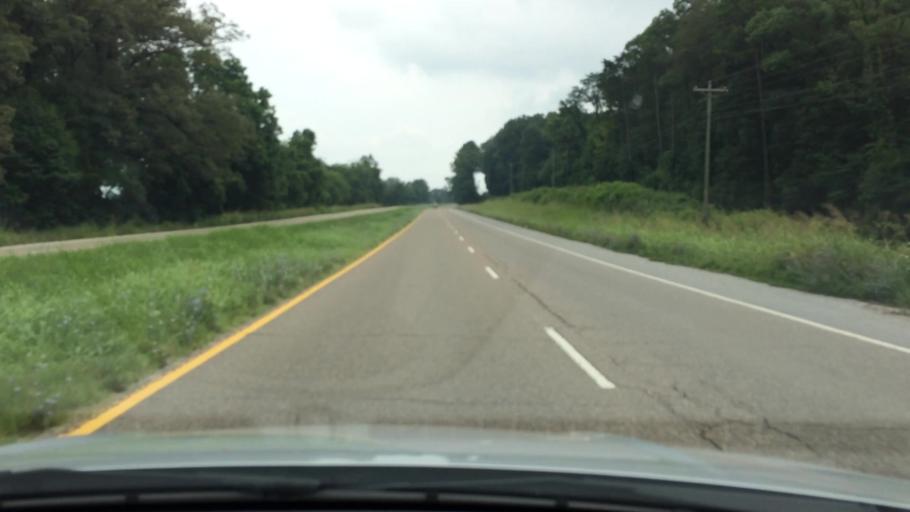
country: US
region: Tennessee
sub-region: Jefferson County
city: New Market
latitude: 36.0819
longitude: -83.6140
